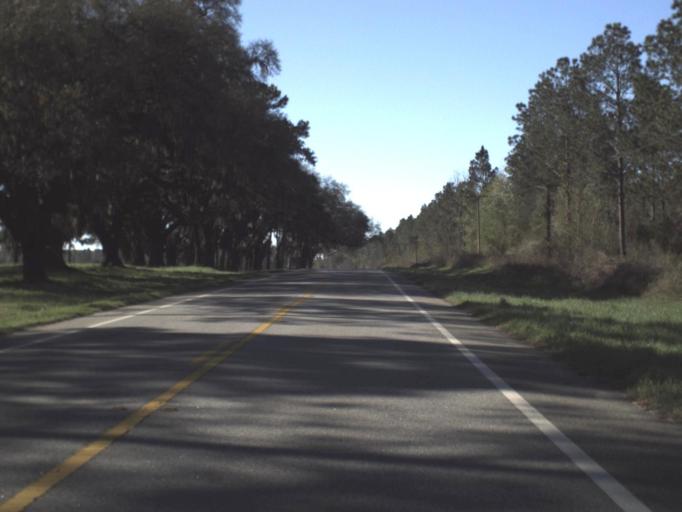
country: US
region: Georgia
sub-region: Brooks County
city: Quitman
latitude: 30.6278
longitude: -83.6462
